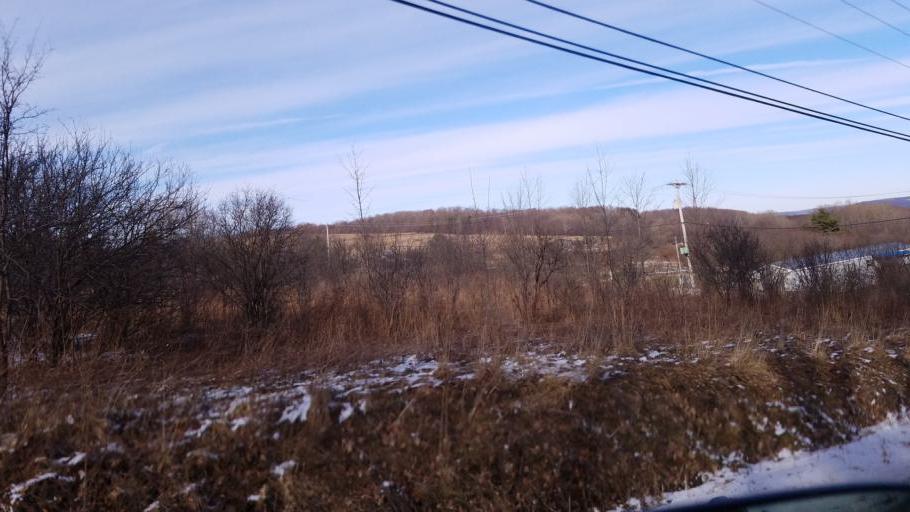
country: US
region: New York
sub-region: Allegany County
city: Wellsville
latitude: 42.0934
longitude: -77.9962
